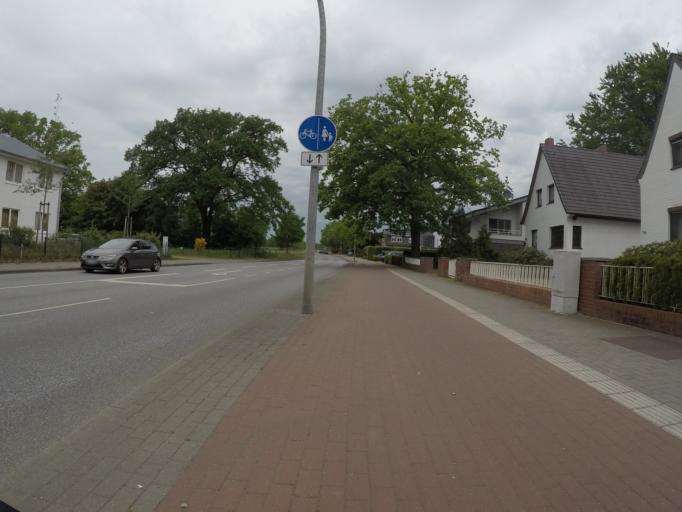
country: DE
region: Schleswig-Holstein
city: Norderstedt
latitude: 53.6903
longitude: 9.9778
